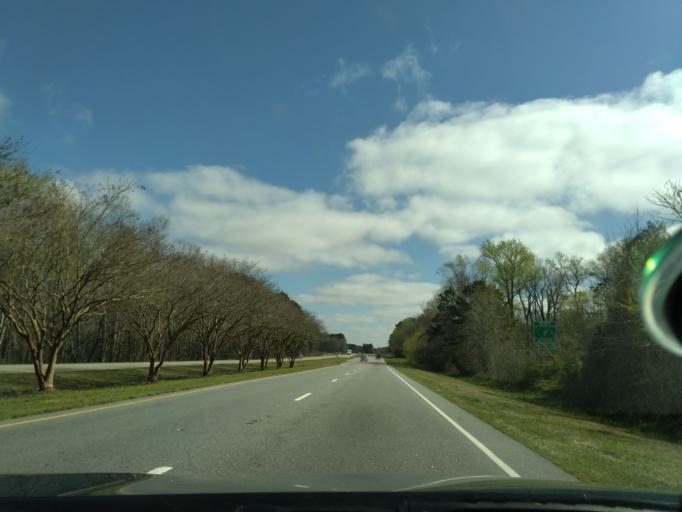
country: US
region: North Carolina
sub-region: Perquimans County
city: Hertford
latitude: 36.1673
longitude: -76.4733
